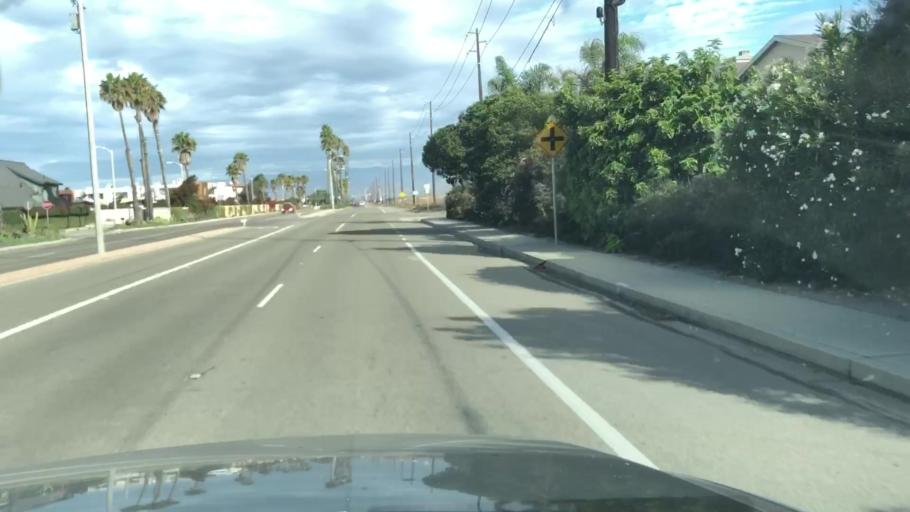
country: US
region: California
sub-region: Ventura County
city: Oxnard Shores
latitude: 34.1937
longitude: -119.2401
